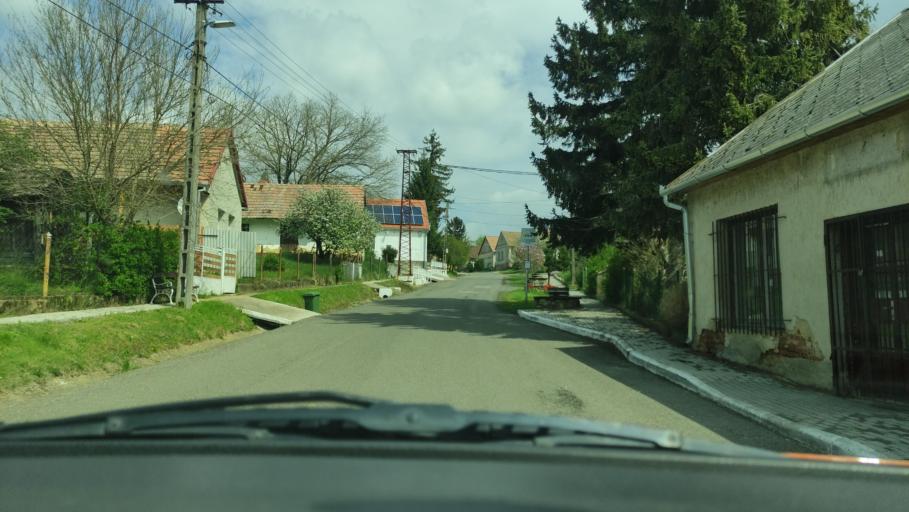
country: HU
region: Baranya
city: Sasd
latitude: 46.2897
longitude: 18.1025
